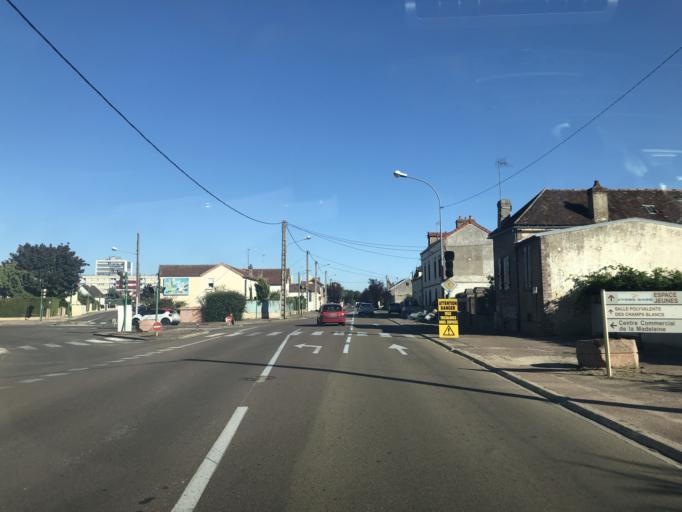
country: FR
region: Bourgogne
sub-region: Departement de l'Yonne
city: Joigny
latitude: 47.9784
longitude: 3.4078
